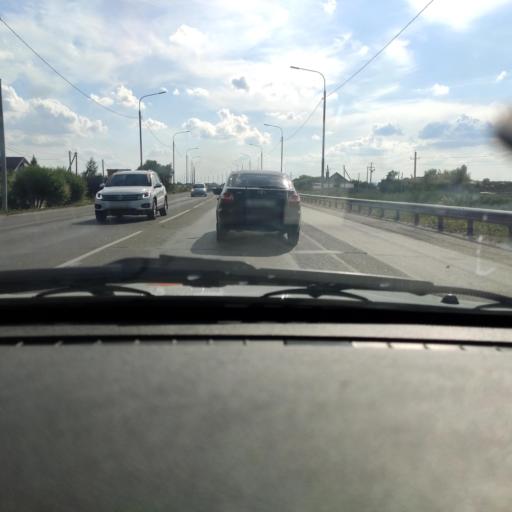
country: RU
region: Voronezj
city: Somovo
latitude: 51.6896
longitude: 39.3607
